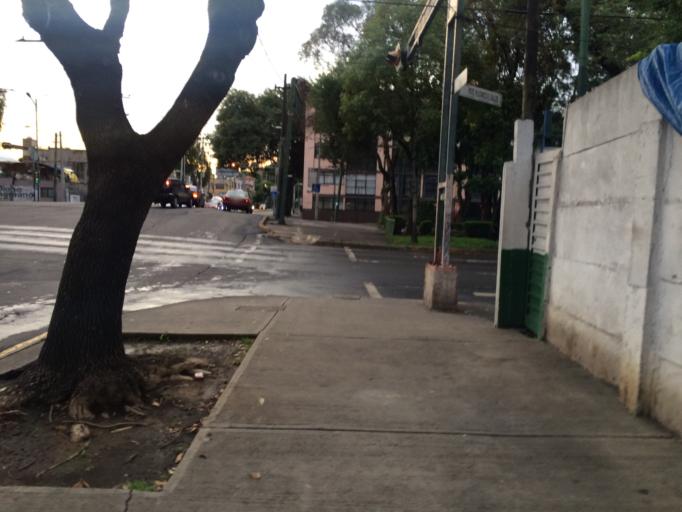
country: MX
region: Mexico City
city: Colonia Nativitas
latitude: 19.3636
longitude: -99.1389
